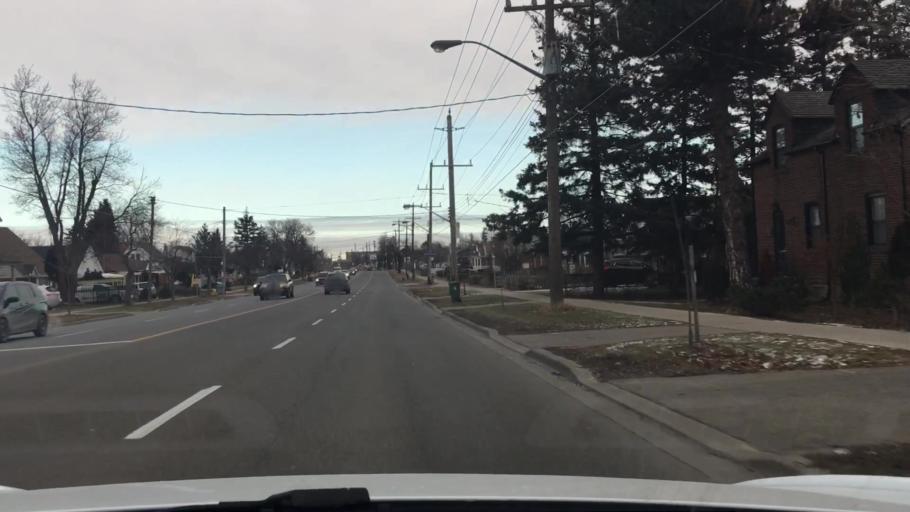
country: CA
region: Ontario
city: Scarborough
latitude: 43.7311
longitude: -79.2505
